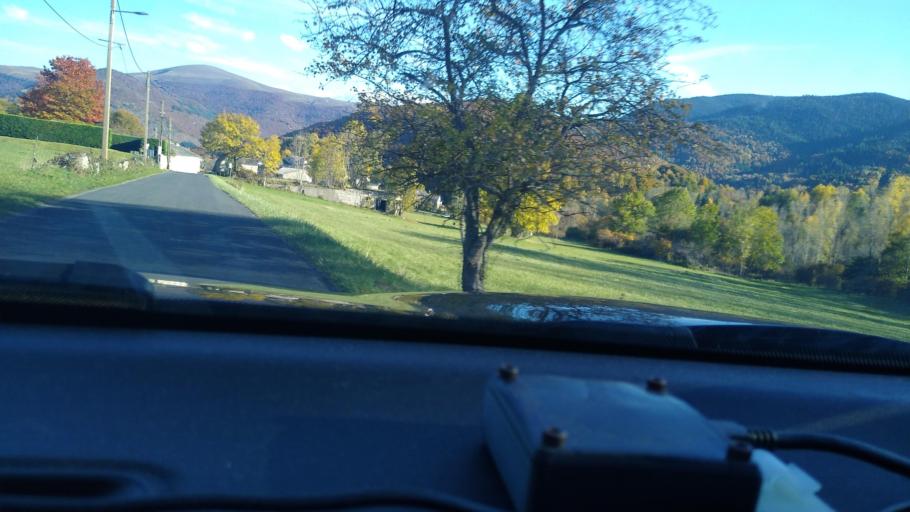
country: FR
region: Languedoc-Roussillon
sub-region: Departement de l'Aude
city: Quillan
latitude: 42.7402
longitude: 2.1973
